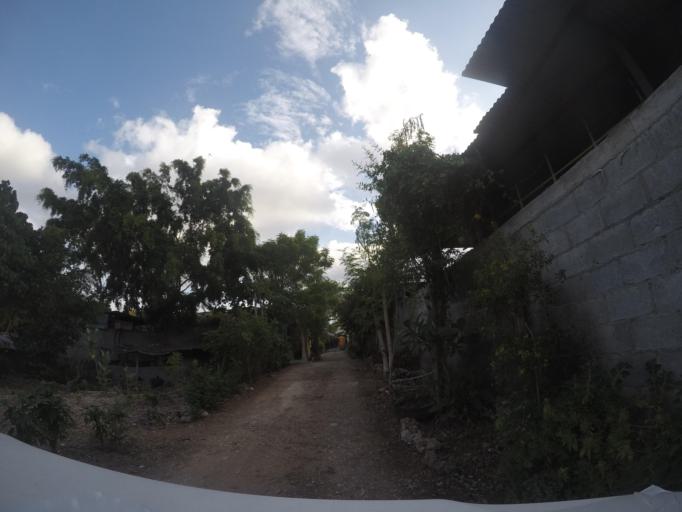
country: TL
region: Baucau
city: Baucau
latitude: -8.4781
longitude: 126.4571
